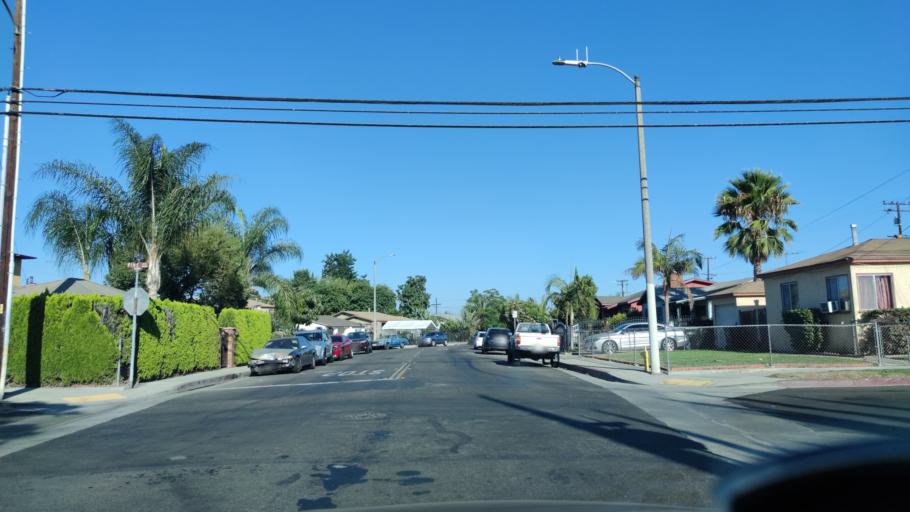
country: US
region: California
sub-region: Los Angeles County
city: Maywood
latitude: 33.9931
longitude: -118.1871
